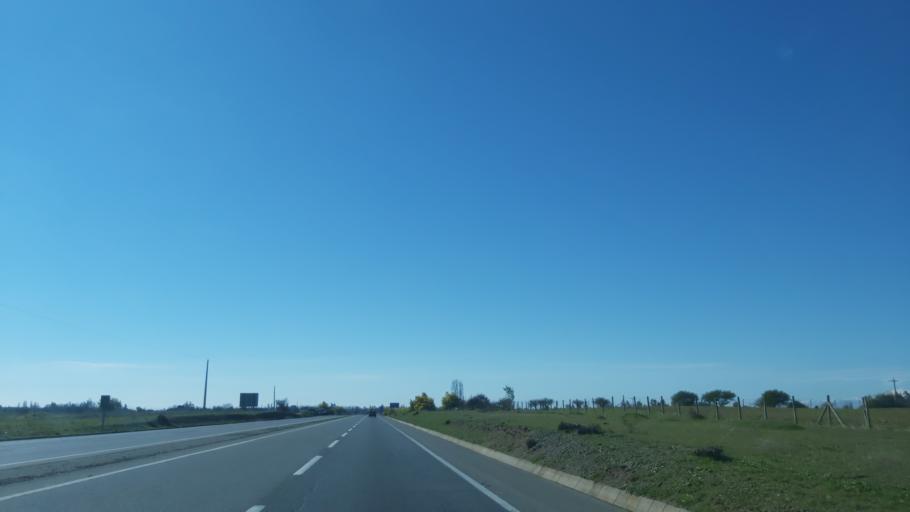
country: CL
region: Biobio
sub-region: Provincia de Nuble
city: Bulnes
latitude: -36.6566
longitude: -72.2460
